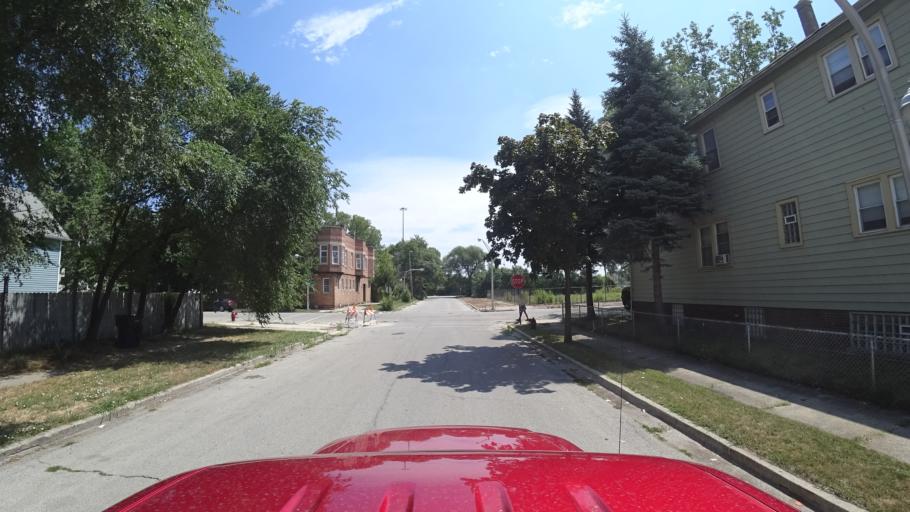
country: US
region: Illinois
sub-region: Cook County
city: Chicago
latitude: 41.8125
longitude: -87.6326
